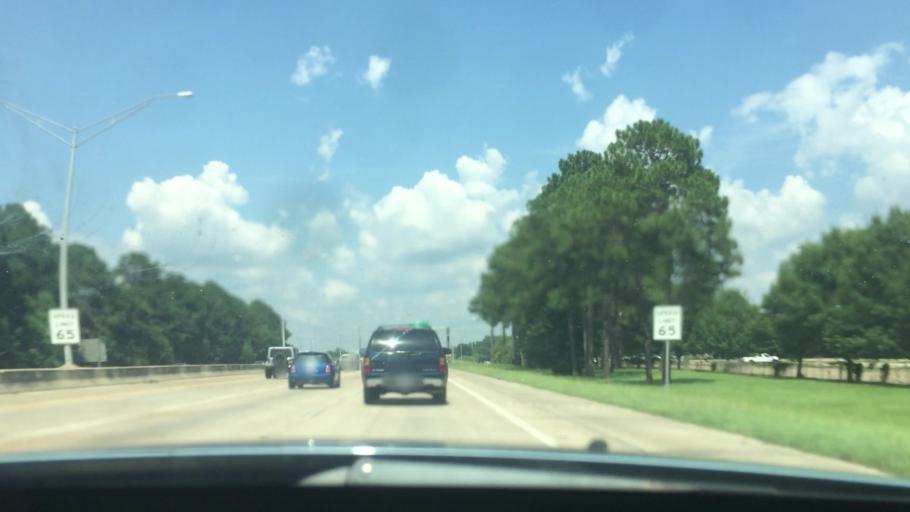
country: US
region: Louisiana
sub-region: East Baton Rouge Parish
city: Shenandoah
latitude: 30.4405
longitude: -91.0145
